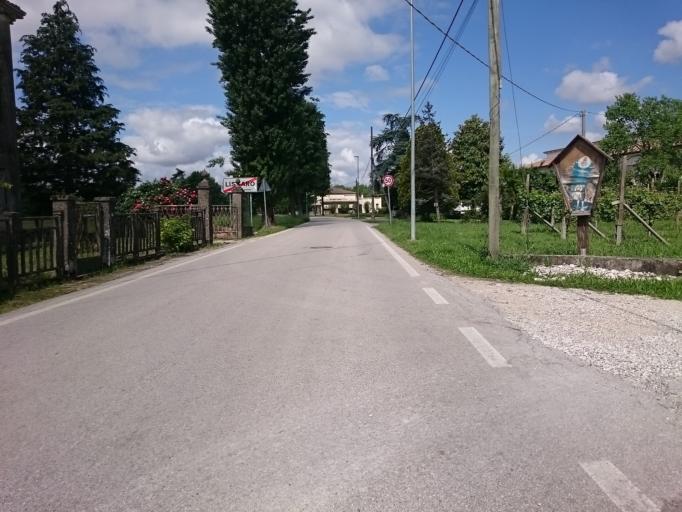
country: IT
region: Veneto
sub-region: Provincia di Padova
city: Arlesega
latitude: 45.4608
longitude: 11.7423
